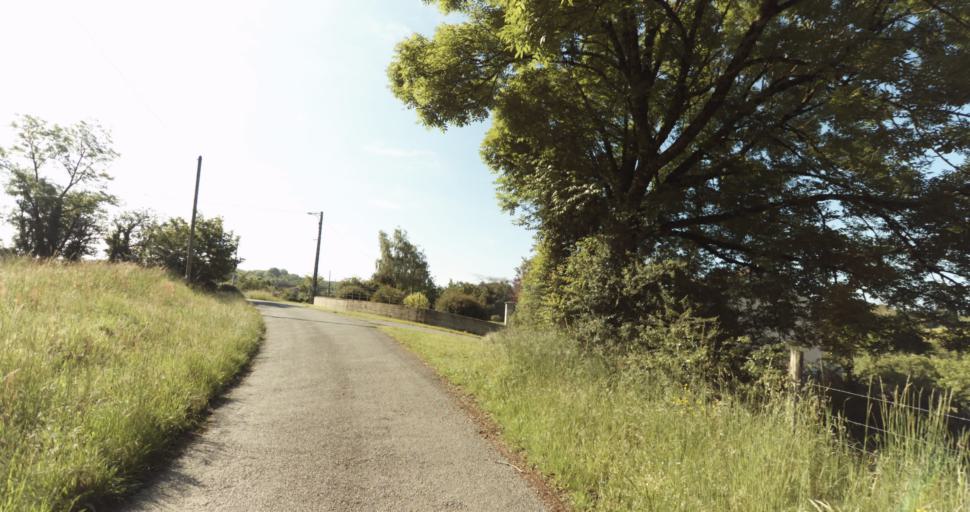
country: FR
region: Limousin
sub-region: Departement de la Haute-Vienne
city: Solignac
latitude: 45.7311
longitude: 1.2425
